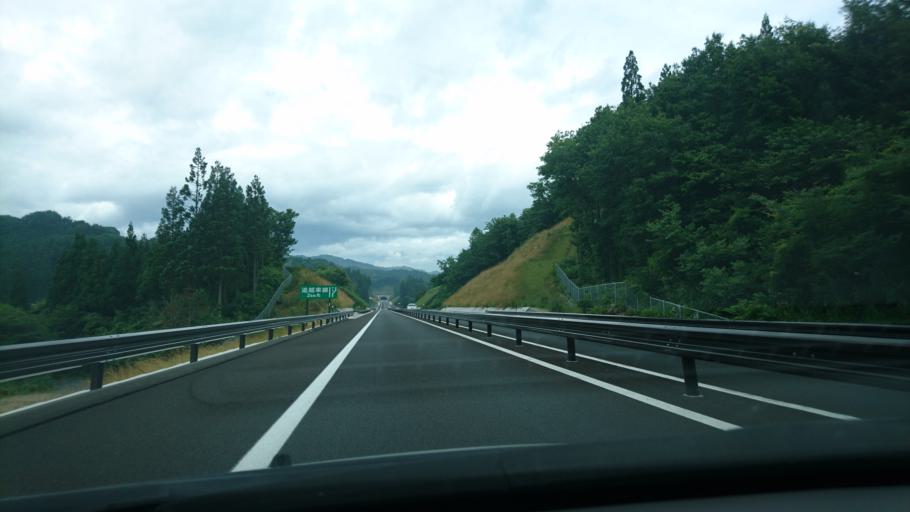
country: JP
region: Iwate
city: Miyako
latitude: 39.5558
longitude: 141.9259
